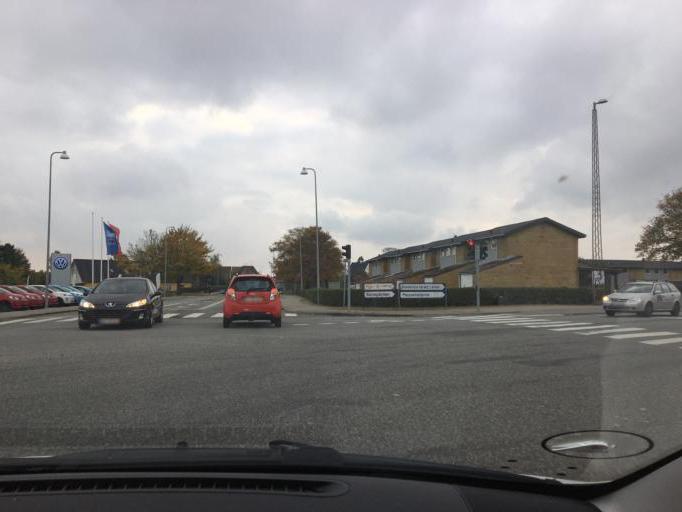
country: DK
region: South Denmark
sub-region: Fredericia Kommune
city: Fredericia
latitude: 55.5785
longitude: 9.7537
